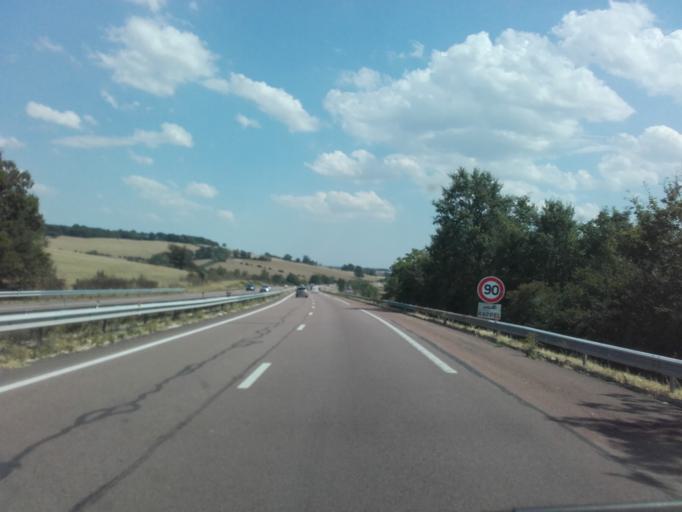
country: FR
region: Bourgogne
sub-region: Departement de l'Yonne
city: Avallon
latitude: 47.5516
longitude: 3.9571
